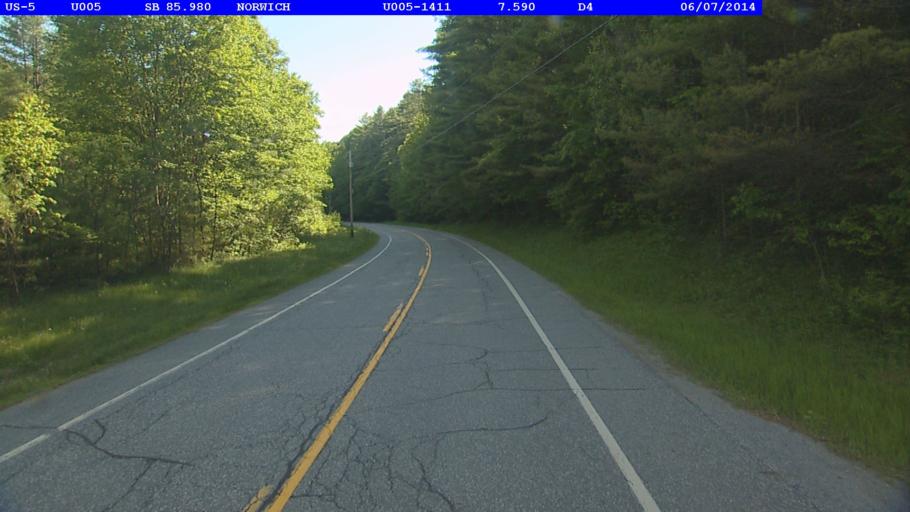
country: US
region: New Hampshire
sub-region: Grafton County
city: Lyme
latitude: 43.7663
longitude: -72.2183
